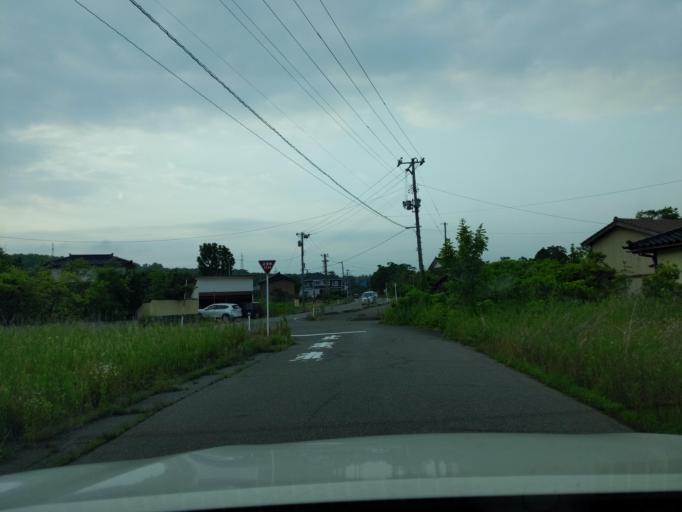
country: JP
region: Niigata
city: Kashiwazaki
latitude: 37.4022
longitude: 138.6002
